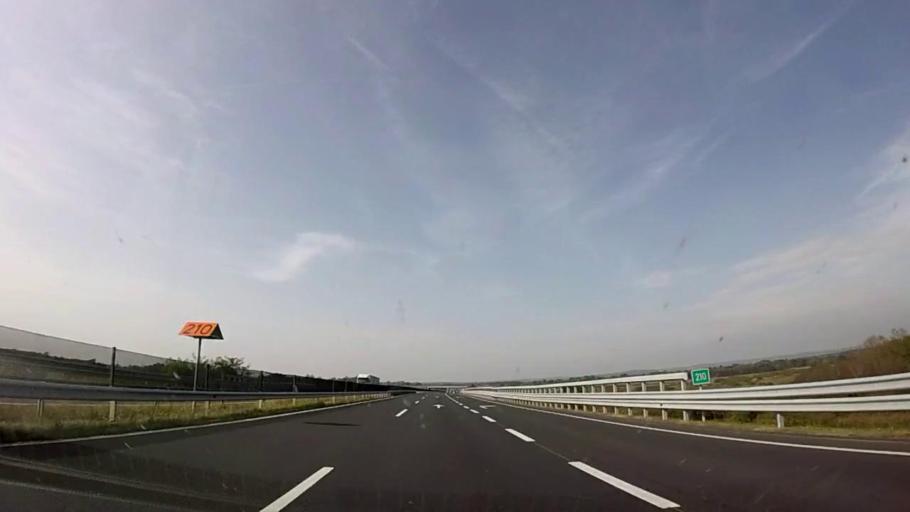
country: HU
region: Zala
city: Nagykanizsa
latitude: 46.4777
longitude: 16.9784
